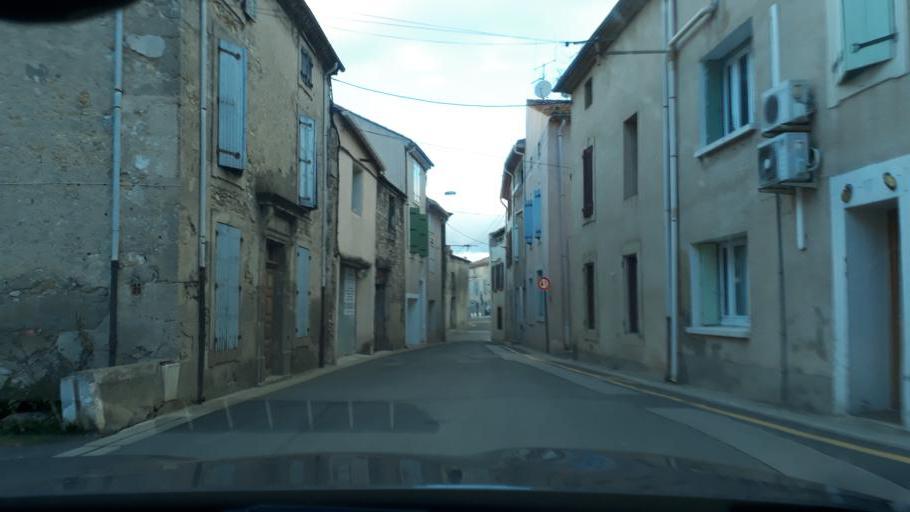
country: FR
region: Languedoc-Roussillon
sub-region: Departement de l'Herault
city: Nissan-lez-Enserune
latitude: 43.2897
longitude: 3.1295
